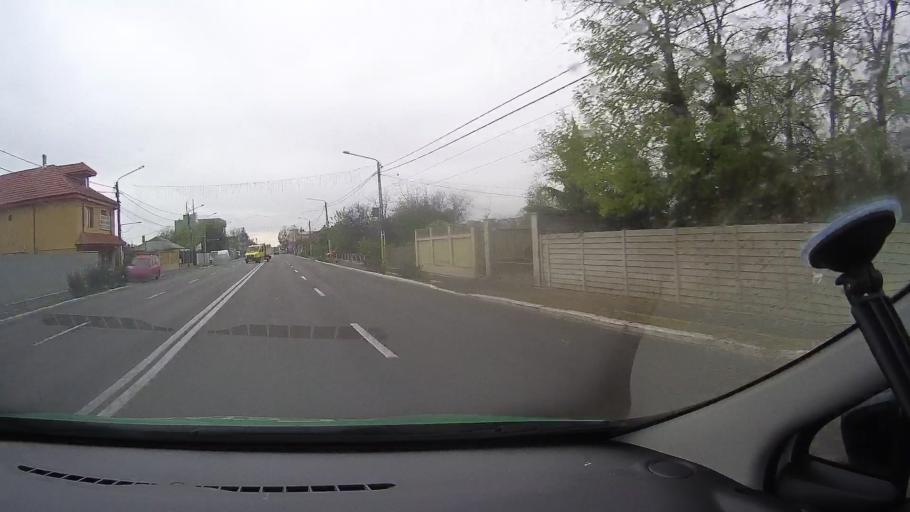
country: RO
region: Constanta
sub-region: Comuna Valu lui Traian
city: Valu lui Traian
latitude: 44.1649
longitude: 28.4870
